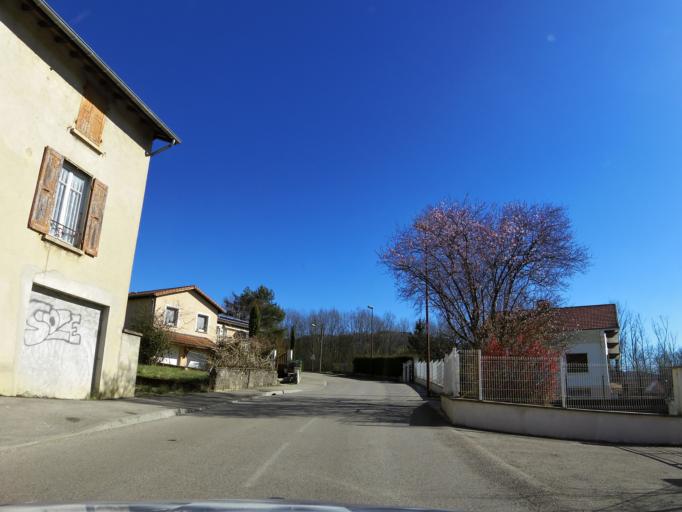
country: FR
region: Rhone-Alpes
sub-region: Departement de l'Ain
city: Amberieu-en-Bugey
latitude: 45.9593
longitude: 5.3621
